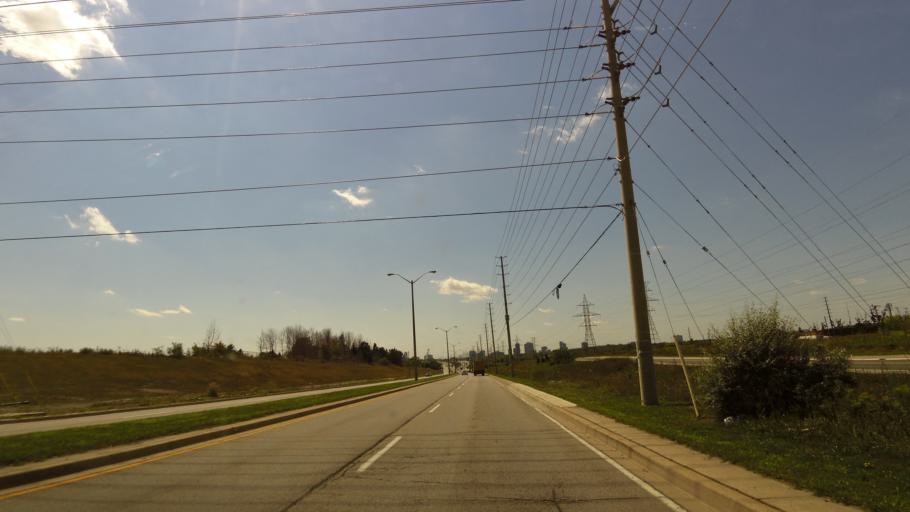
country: CA
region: Ontario
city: Etobicoke
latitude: 43.6292
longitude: -79.6152
